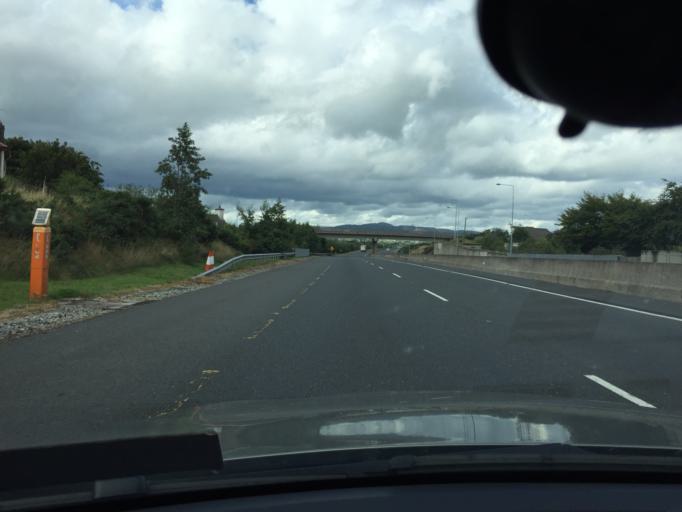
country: GB
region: Northern Ireland
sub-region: Newry and Mourne District
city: Newry
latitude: 54.0964
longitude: -6.3618
